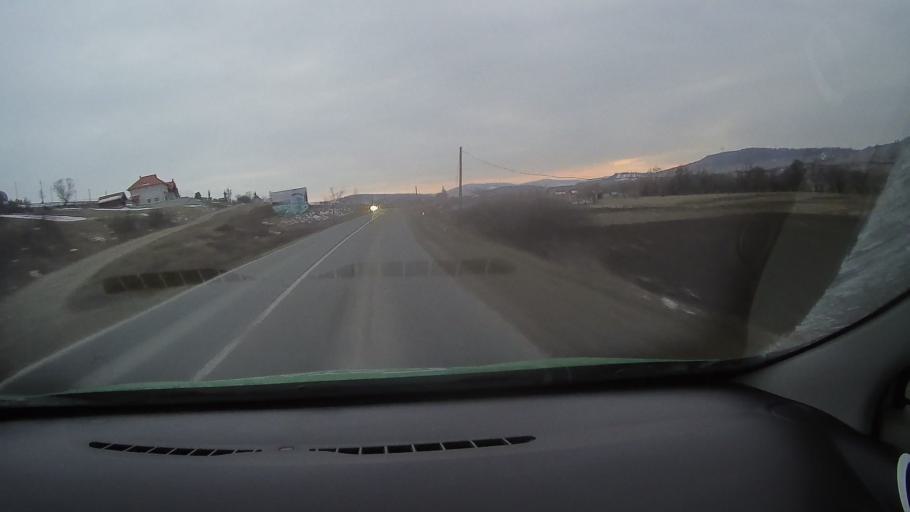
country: RO
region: Harghita
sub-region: Municipiul Odorheiu Secuiesc
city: Odorheiu Secuiesc
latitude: 46.2798
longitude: 25.2885
